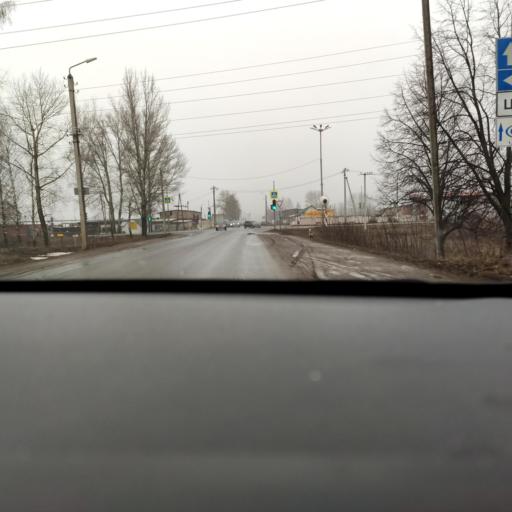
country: RU
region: Tatarstan
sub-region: Chistopol'skiy Rayon
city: Chistopol'
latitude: 55.3512
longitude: 50.6675
